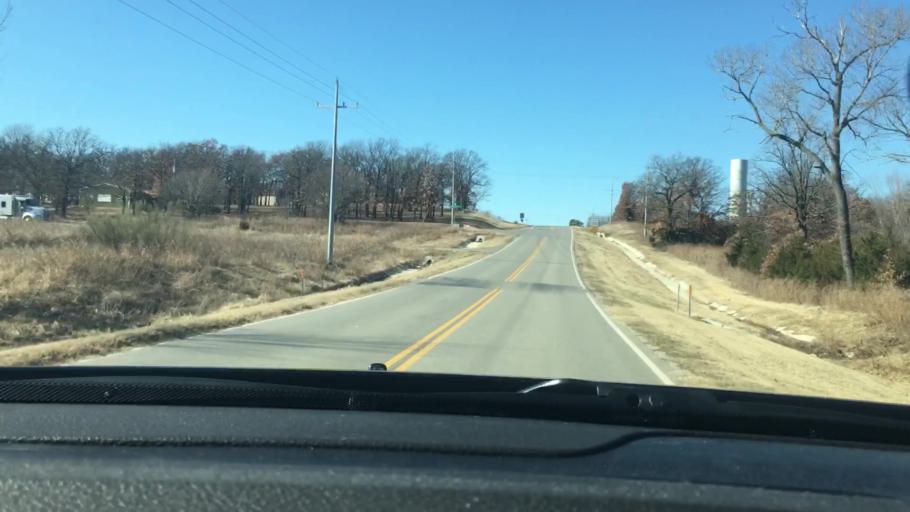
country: US
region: Oklahoma
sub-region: Murray County
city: Davis
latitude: 34.4771
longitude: -97.0454
